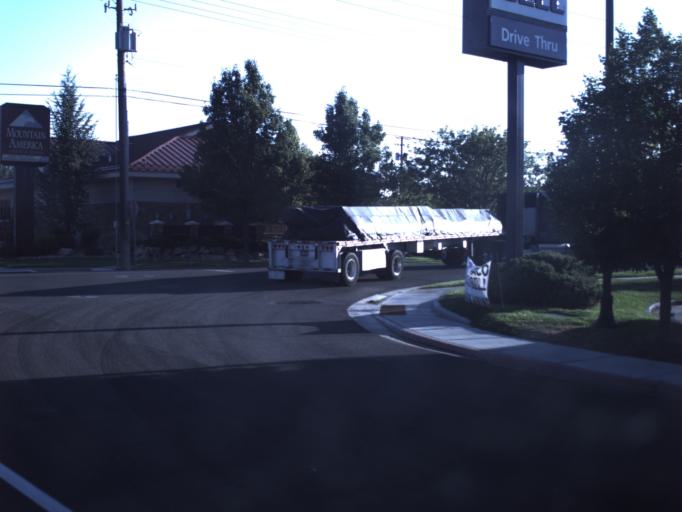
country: US
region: Utah
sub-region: Utah County
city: Spanish Fork
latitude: 40.1217
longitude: -111.6548
